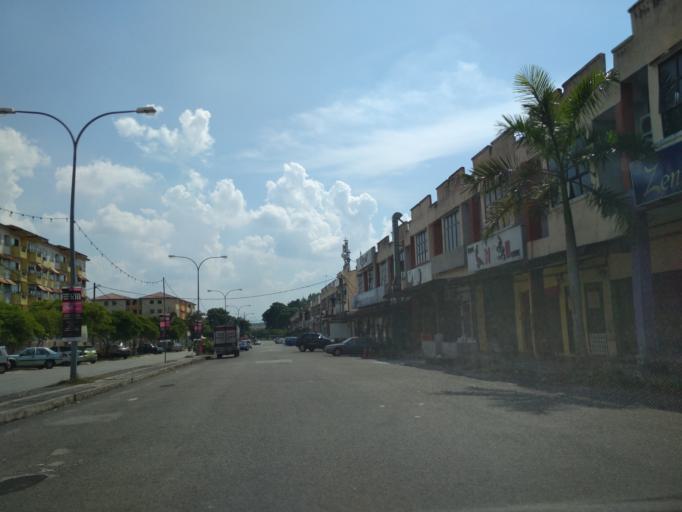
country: MY
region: Perak
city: Kampar
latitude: 4.3305
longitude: 101.1460
